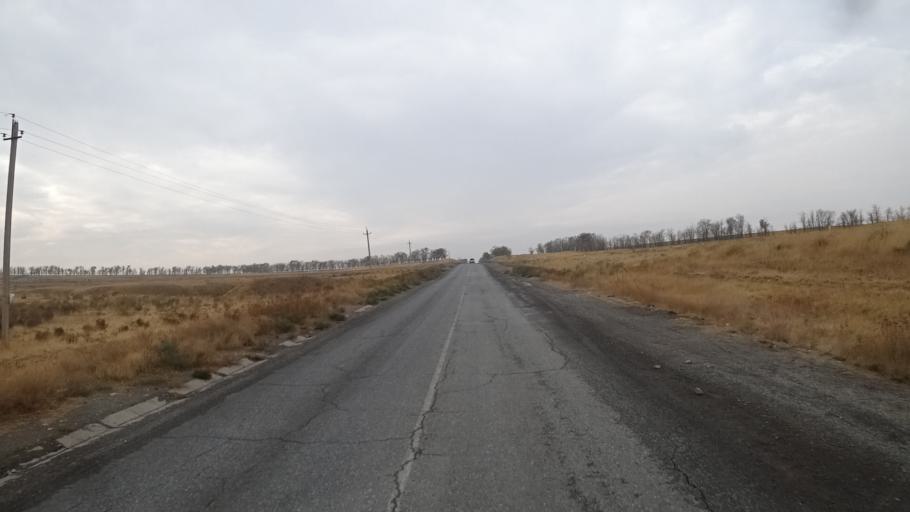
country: KZ
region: Ongtustik Qazaqstan
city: Aksu
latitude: 42.4206
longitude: 69.6938
